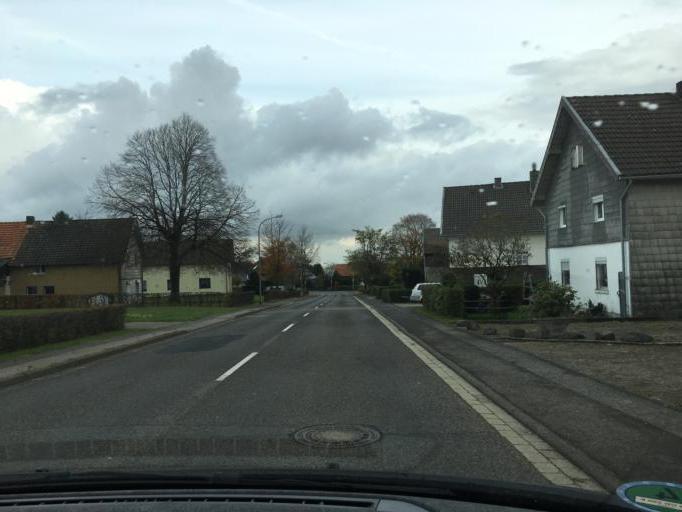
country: DE
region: North Rhine-Westphalia
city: Heimbach
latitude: 50.6579
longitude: 6.4044
